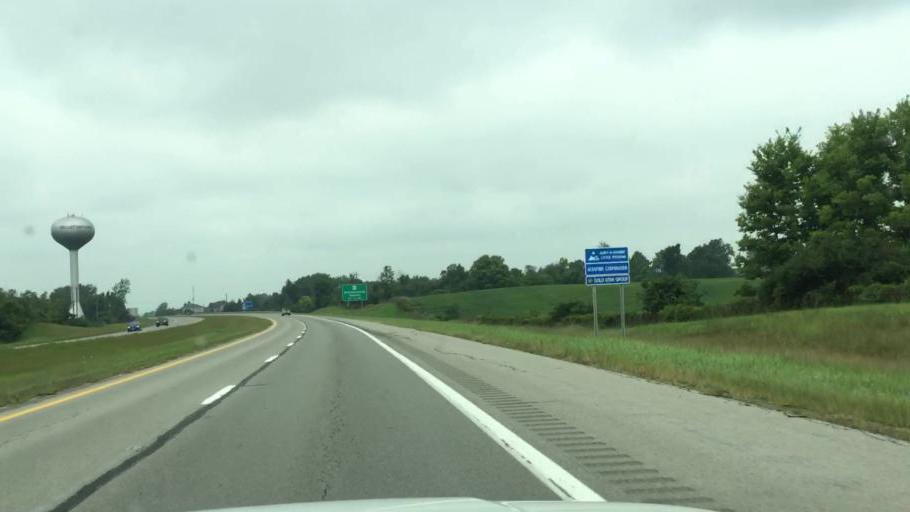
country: US
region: Ohio
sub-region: Logan County
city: Bellefontaine
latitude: 40.3768
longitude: -83.7417
